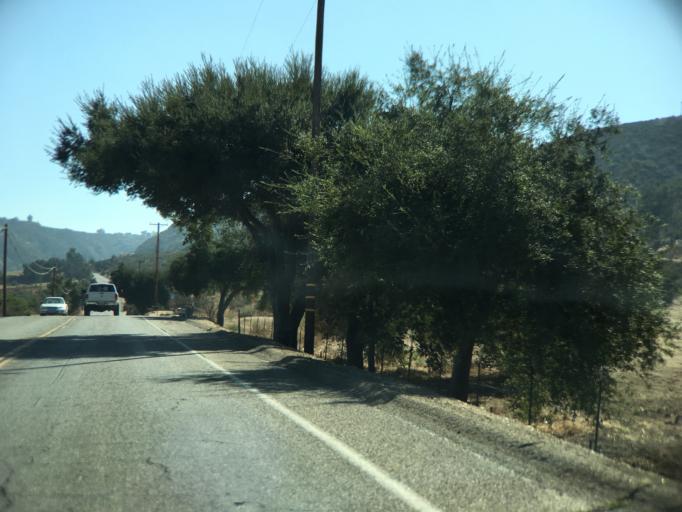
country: US
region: California
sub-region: San Diego County
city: Valley Center
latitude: 33.2485
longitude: -116.9635
